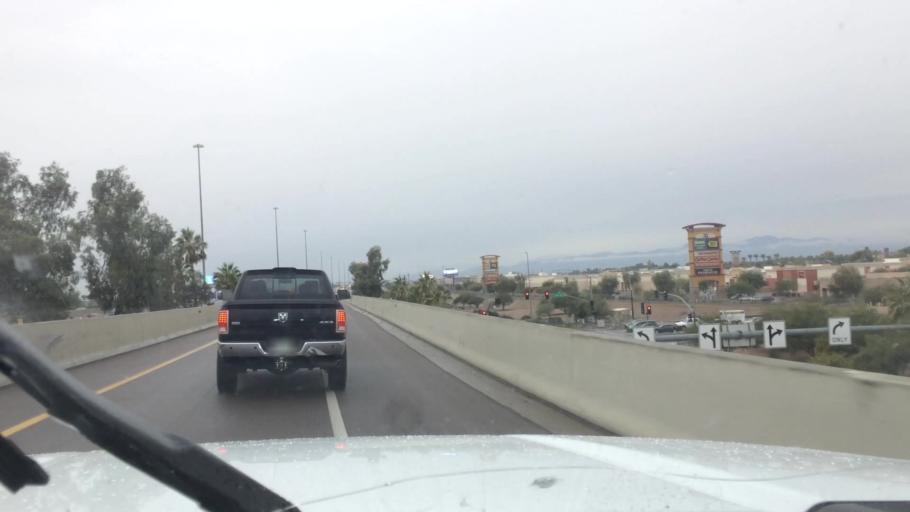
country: US
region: Arizona
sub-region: Maricopa County
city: Tolleson
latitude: 33.4621
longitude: -112.2712
